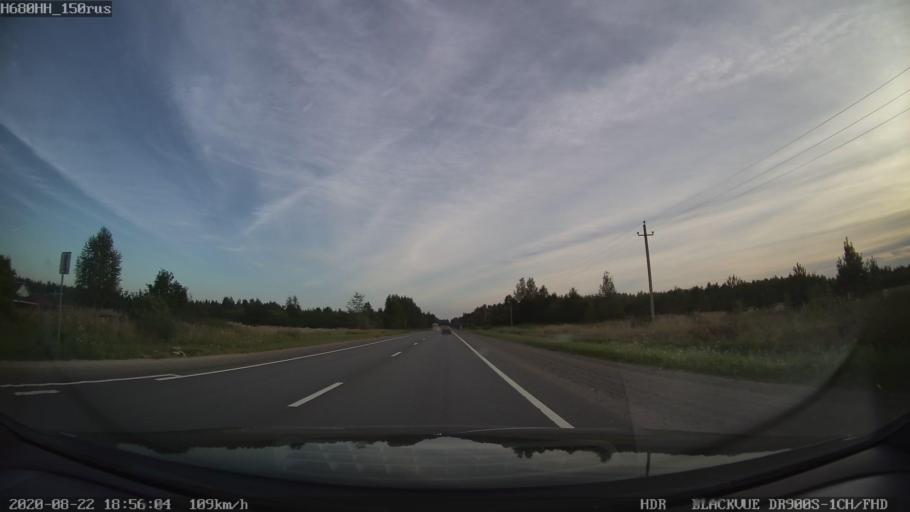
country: RU
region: Tverskaya
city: Rameshki
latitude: 57.1900
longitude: 36.0834
